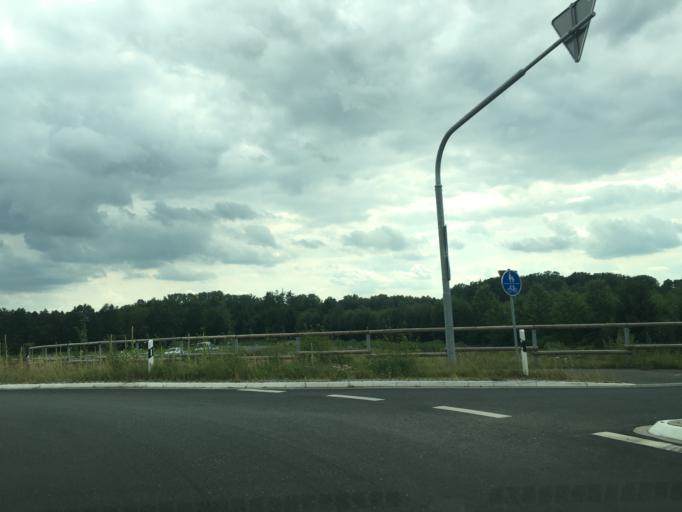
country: DE
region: North Rhine-Westphalia
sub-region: Regierungsbezirk Munster
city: Telgte
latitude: 51.8985
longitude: 7.7353
